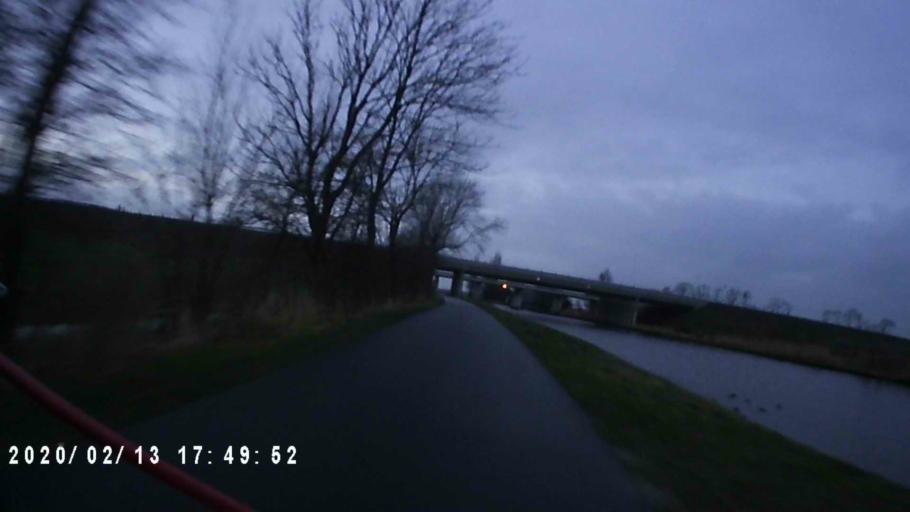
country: NL
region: Groningen
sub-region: Gemeente Zuidhorn
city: Aduard
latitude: 53.2439
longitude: 6.4795
